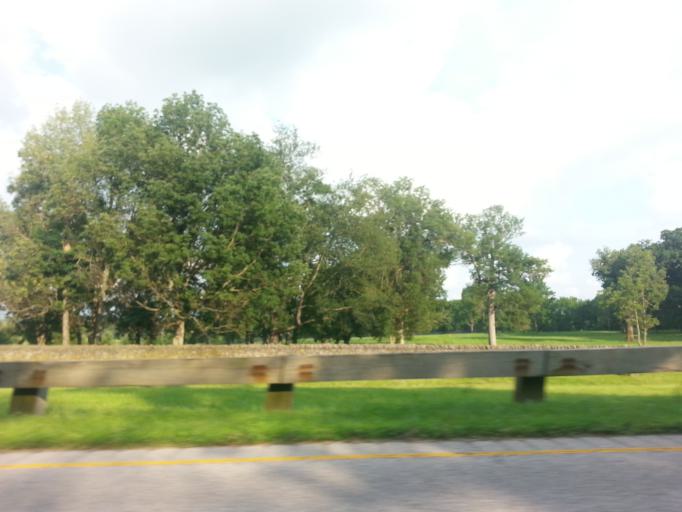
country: US
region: Kentucky
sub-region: Bourbon County
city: Paris
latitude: 38.1639
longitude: -84.3221
